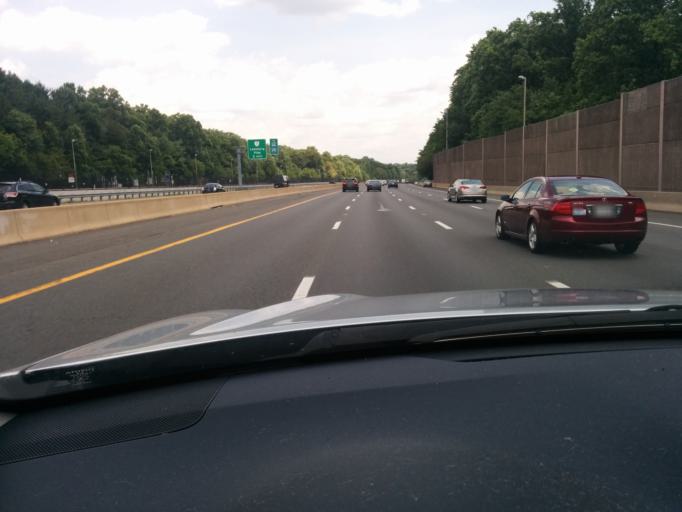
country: US
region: Virginia
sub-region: Fairfax County
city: Wolf Trap
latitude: 38.9478
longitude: -77.3042
